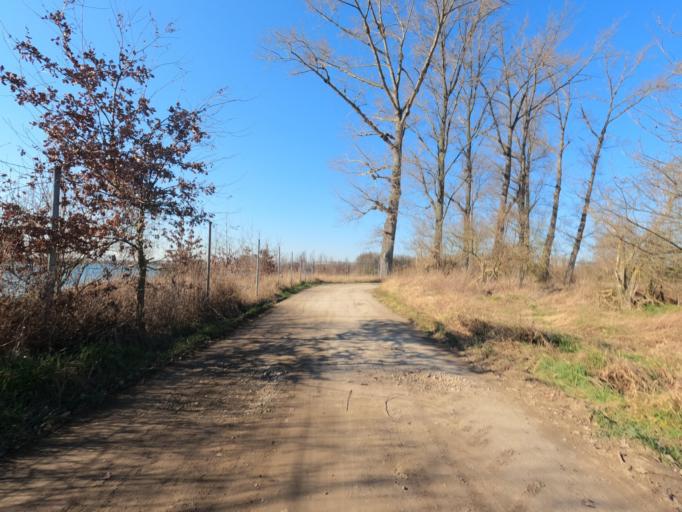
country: DE
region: North Rhine-Westphalia
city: Huckelhoven
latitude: 51.0263
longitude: 6.2539
